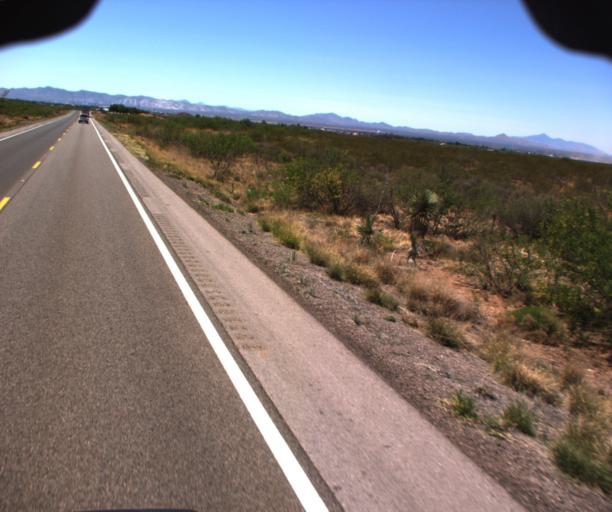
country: US
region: Arizona
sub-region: Cochise County
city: Douglas
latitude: 31.3884
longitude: -109.5133
